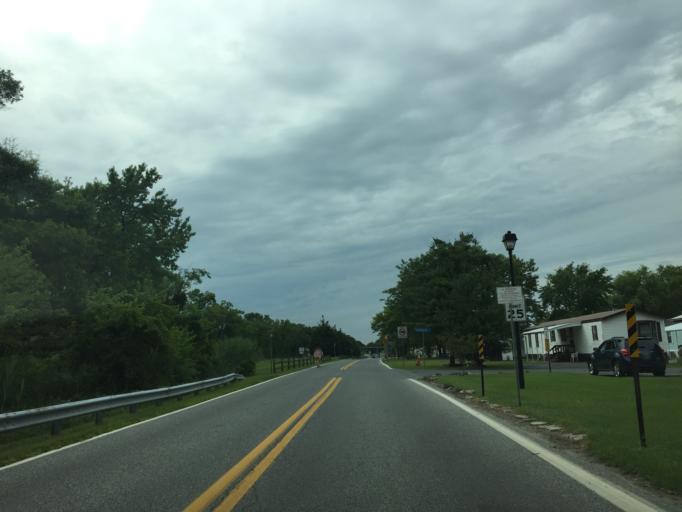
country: US
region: Maryland
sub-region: Baltimore County
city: Essex
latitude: 39.2765
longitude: -76.4651
